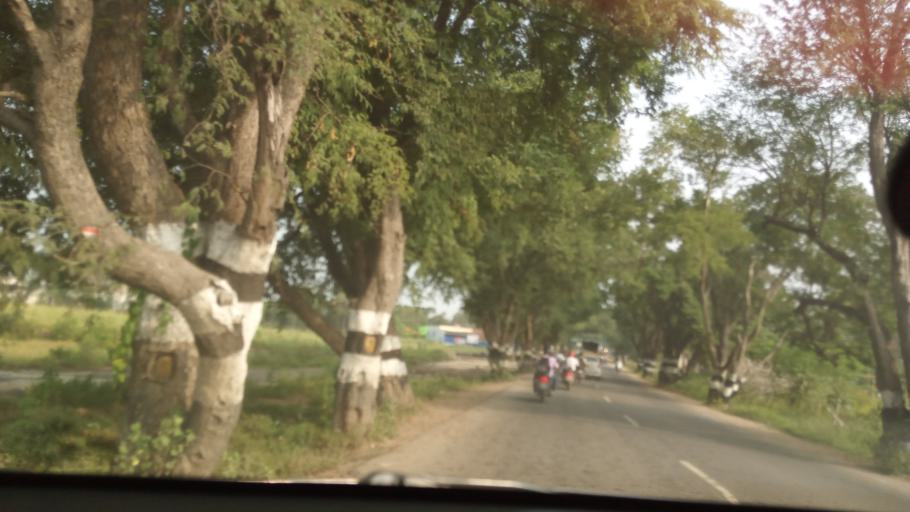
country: IN
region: Tamil Nadu
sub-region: Coimbatore
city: Periyanayakkanpalaiyam
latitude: 11.1549
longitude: 77.0498
